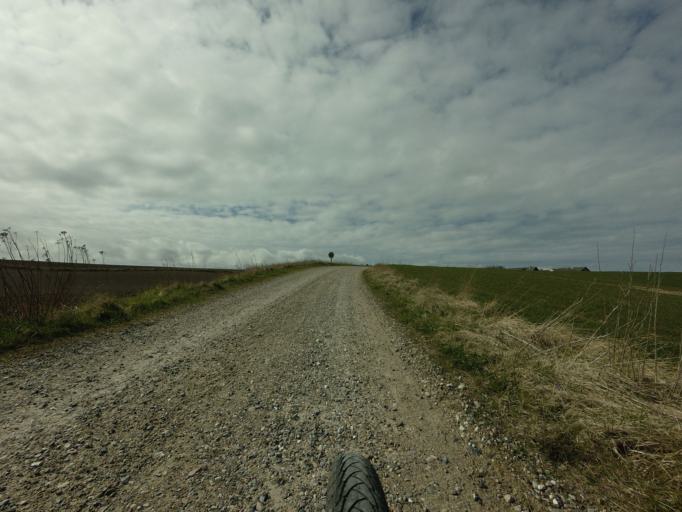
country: DK
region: North Denmark
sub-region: Jammerbugt Kommune
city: Pandrup
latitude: 57.3846
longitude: 9.7405
